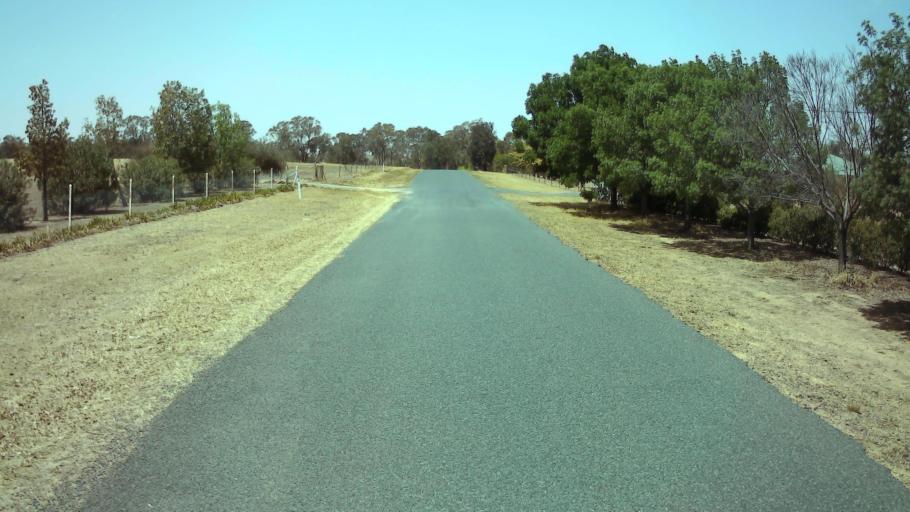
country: AU
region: New South Wales
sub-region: Weddin
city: Grenfell
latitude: -33.9086
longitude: 148.1507
